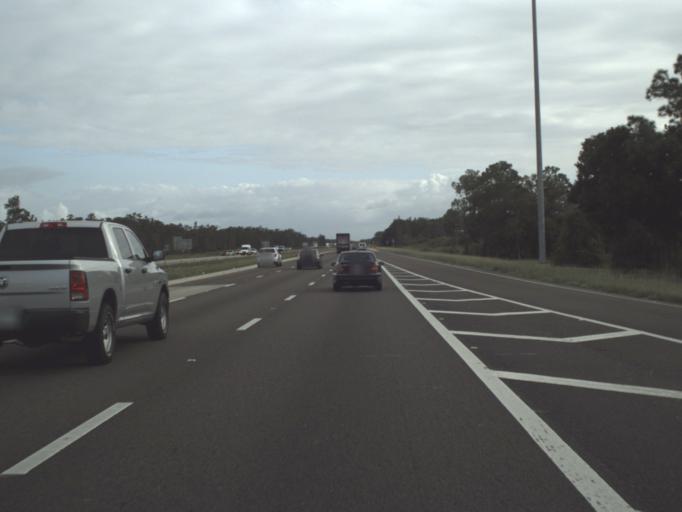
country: US
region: Florida
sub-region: Lee County
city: Fort Myers
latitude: 26.6093
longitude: -81.8024
